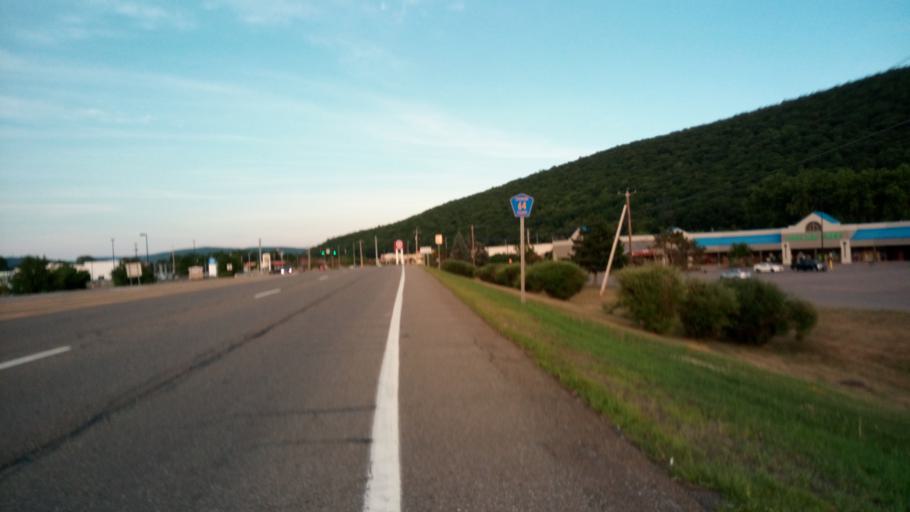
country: US
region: New York
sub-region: Chemung County
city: Horseheads
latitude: 42.1541
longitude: -76.8769
